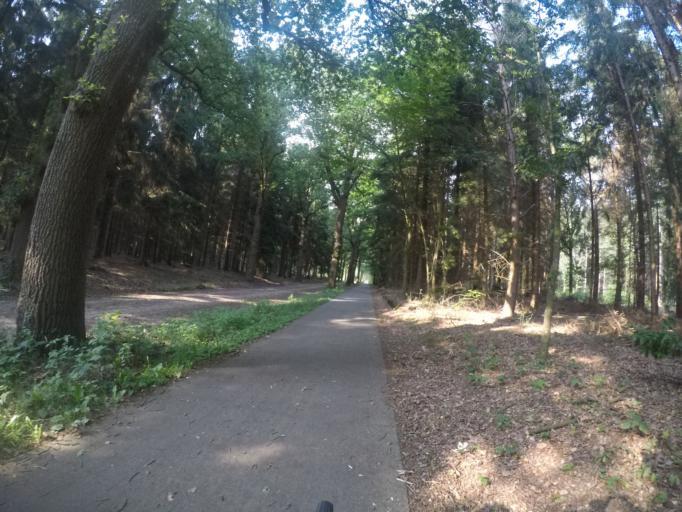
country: NL
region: Friesland
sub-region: Gemeente Weststellingwerf
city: Noordwolde
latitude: 52.8892
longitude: 6.2194
